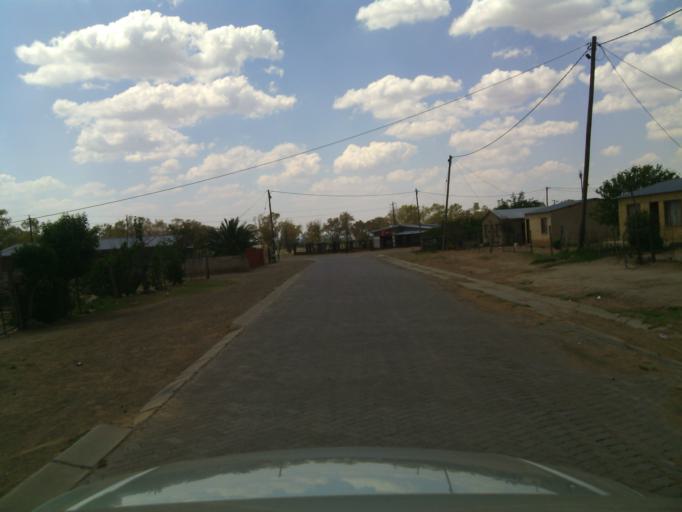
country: ZA
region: Orange Free State
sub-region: Xhariep District Municipality
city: Dewetsdorp
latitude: -29.5775
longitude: 26.6805
